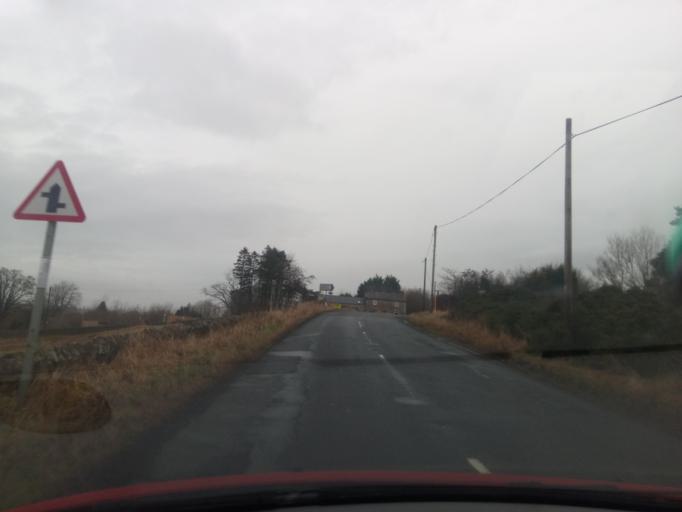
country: GB
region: England
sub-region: Northumberland
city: Rochester
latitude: 55.1643
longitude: -2.3281
